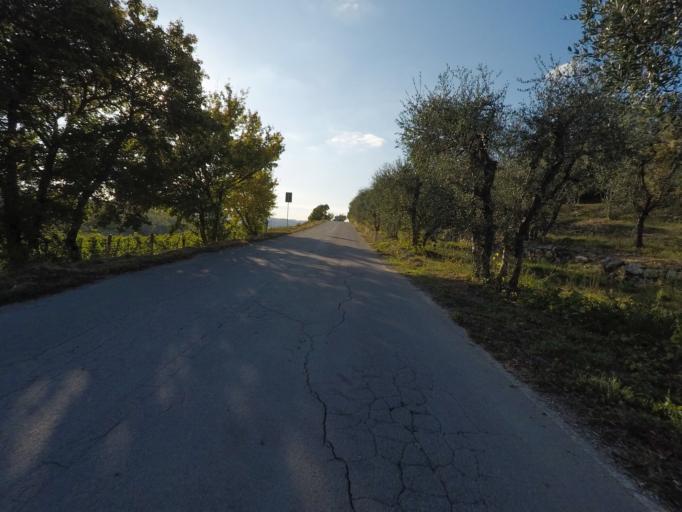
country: IT
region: Tuscany
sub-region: Provincia di Siena
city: Radda in Chianti
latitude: 43.4518
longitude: 11.3895
